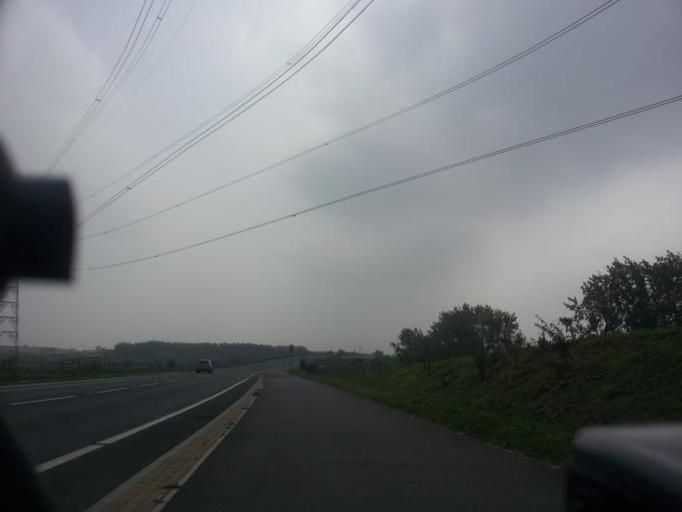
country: GB
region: England
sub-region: Kent
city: Sittingbourne
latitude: 51.3590
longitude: 0.7512
